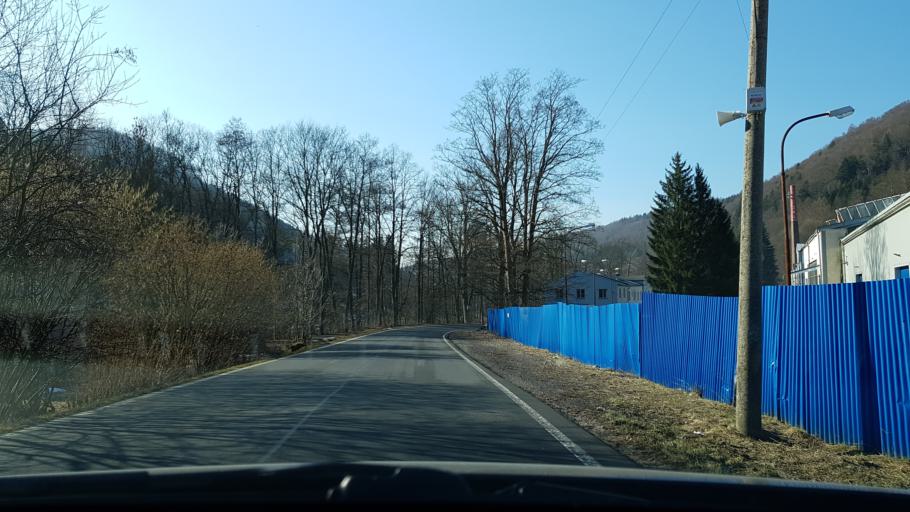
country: CZ
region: Olomoucky
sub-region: Okres Sumperk
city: Hanusovice
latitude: 50.0605
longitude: 16.9242
